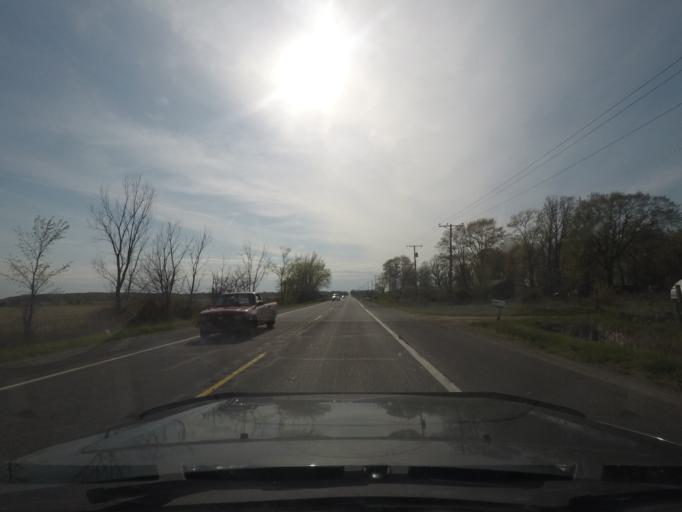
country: US
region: Michigan
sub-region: Berrien County
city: Three Oaks
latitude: 41.7986
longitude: -86.5844
